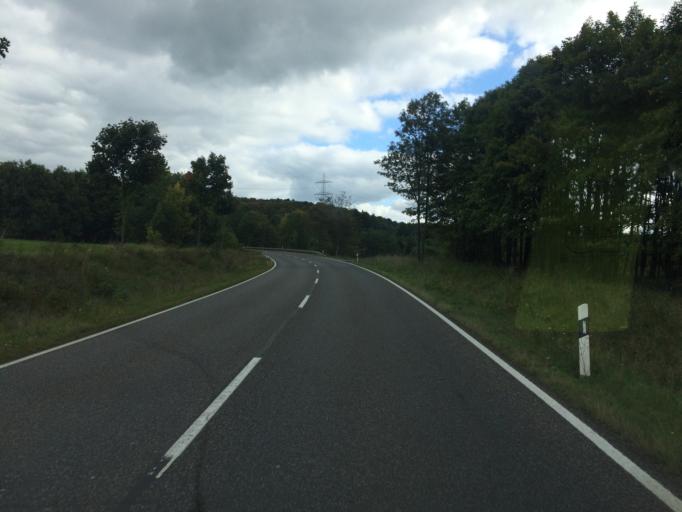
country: DE
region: Rheinland-Pfalz
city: Hellenhahn-Schellenberg
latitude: 50.6097
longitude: 8.0407
